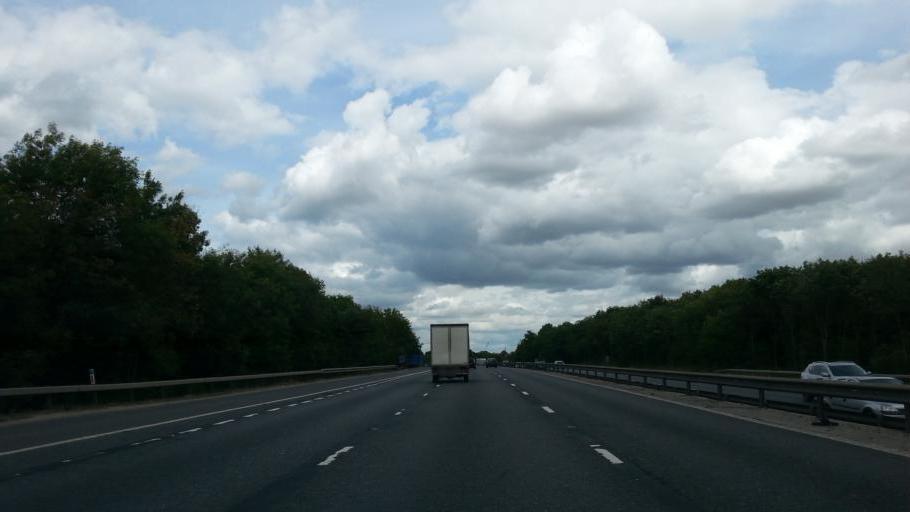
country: GB
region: England
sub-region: Essex
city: Harlow
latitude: 51.7479
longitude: 0.1415
